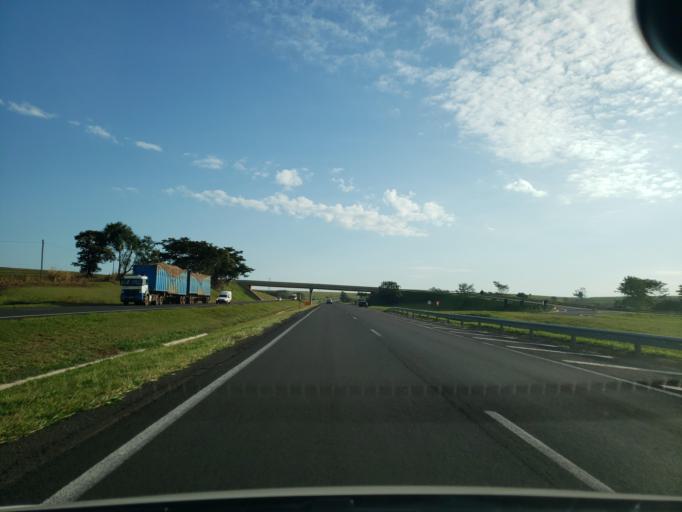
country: BR
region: Sao Paulo
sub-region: Valparaiso
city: Valparaiso
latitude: -21.2144
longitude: -50.8369
